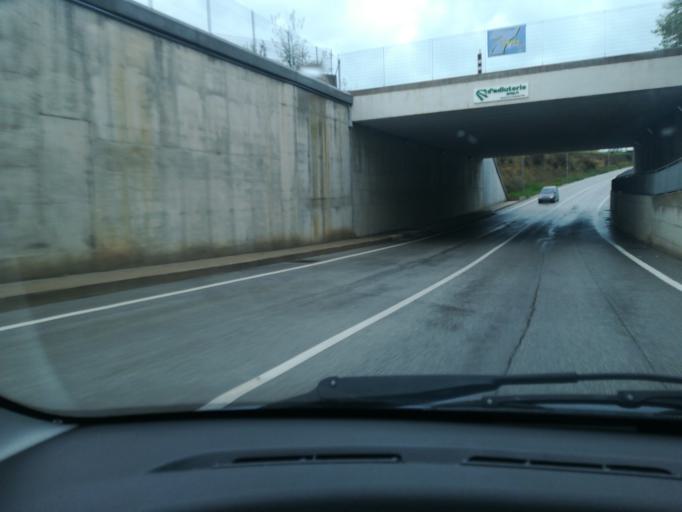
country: IT
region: The Marches
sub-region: Provincia di Macerata
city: Borgo Stazione
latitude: 43.2895
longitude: 13.6525
